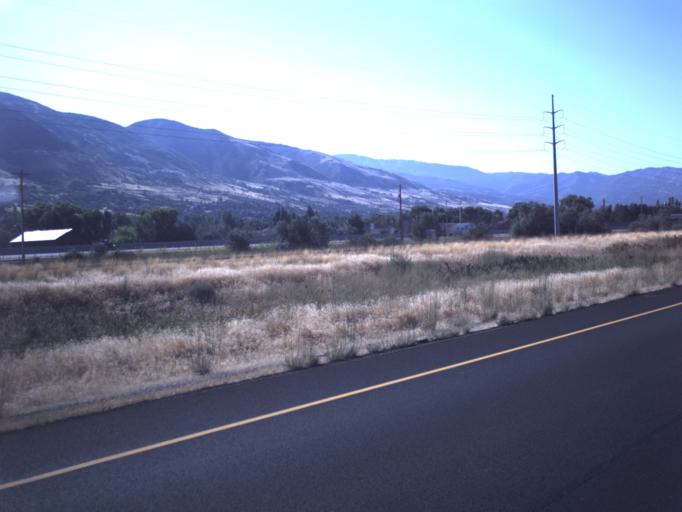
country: US
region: Utah
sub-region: Davis County
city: Farmington
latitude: 40.9516
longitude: -111.8932
